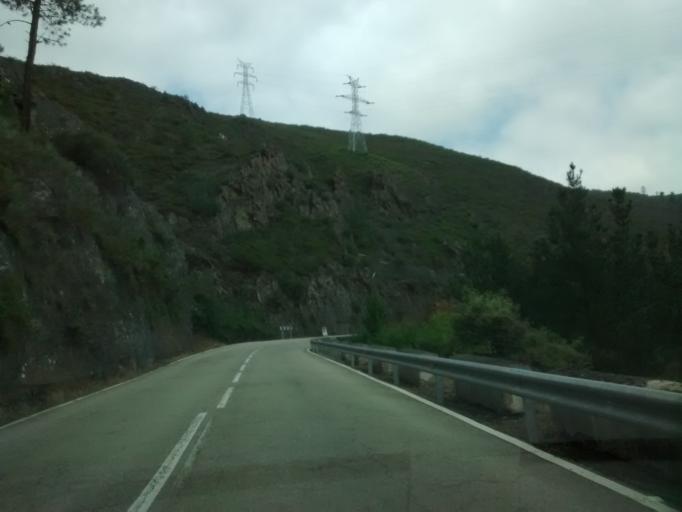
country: ES
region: Galicia
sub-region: Provincia de Ourense
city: Manzaneda
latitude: 42.3346
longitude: -7.2026
